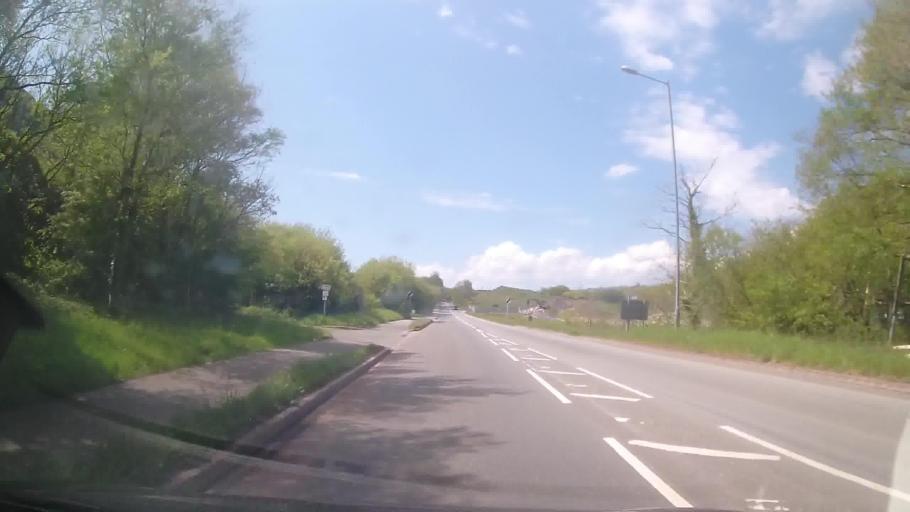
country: GB
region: Wales
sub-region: Gwynedd
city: Porthmadog
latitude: 52.9321
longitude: -4.1473
